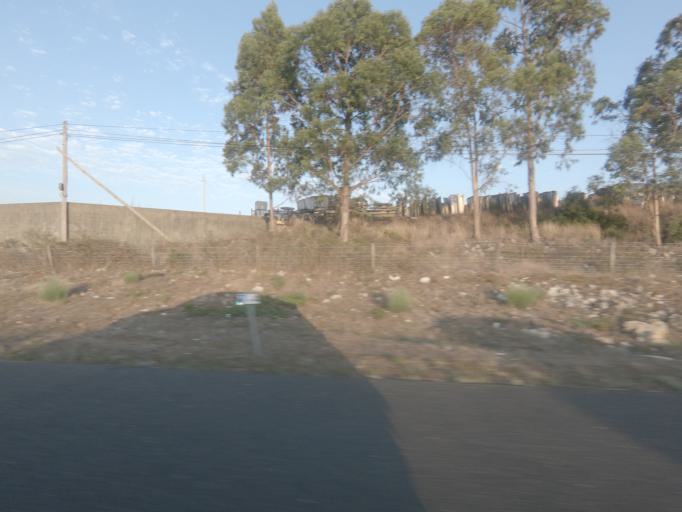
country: PT
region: Leiria
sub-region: Leiria
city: Santa Catarina da Serra
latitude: 39.6659
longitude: -8.6887
